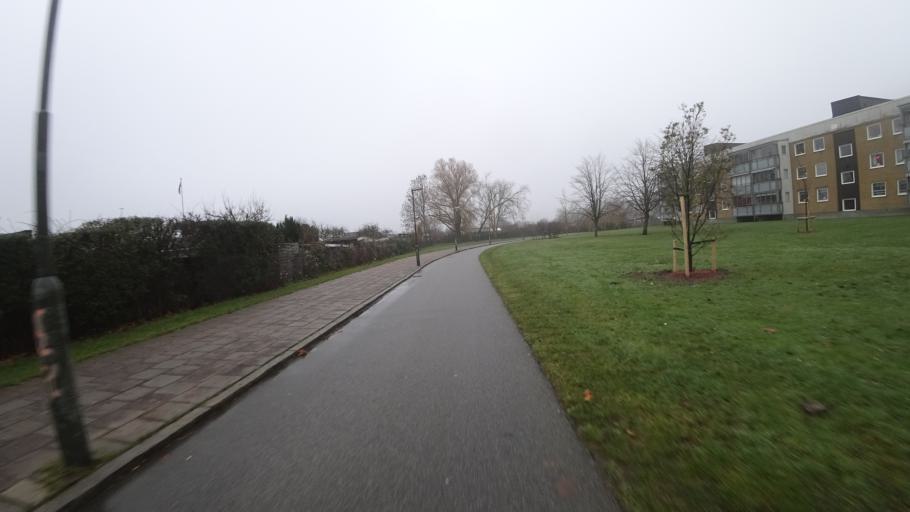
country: SE
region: Skane
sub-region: Malmo
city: Malmoe
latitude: 55.5774
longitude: 12.9881
